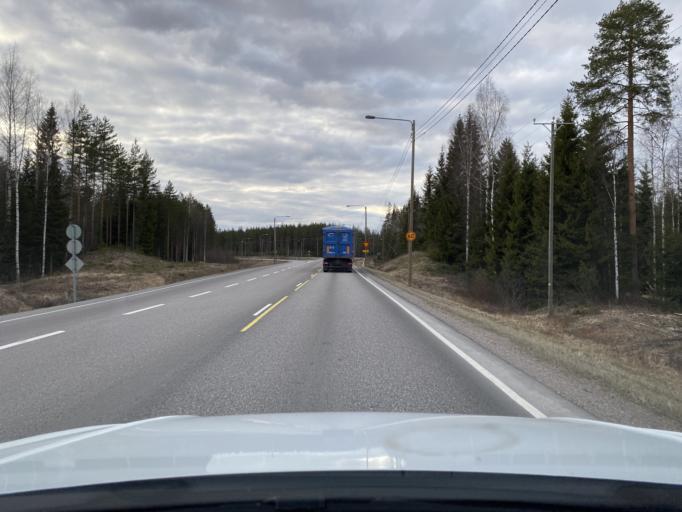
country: FI
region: Uusimaa
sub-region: Helsinki
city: Kaerkoelae
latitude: 60.8266
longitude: 24.0208
